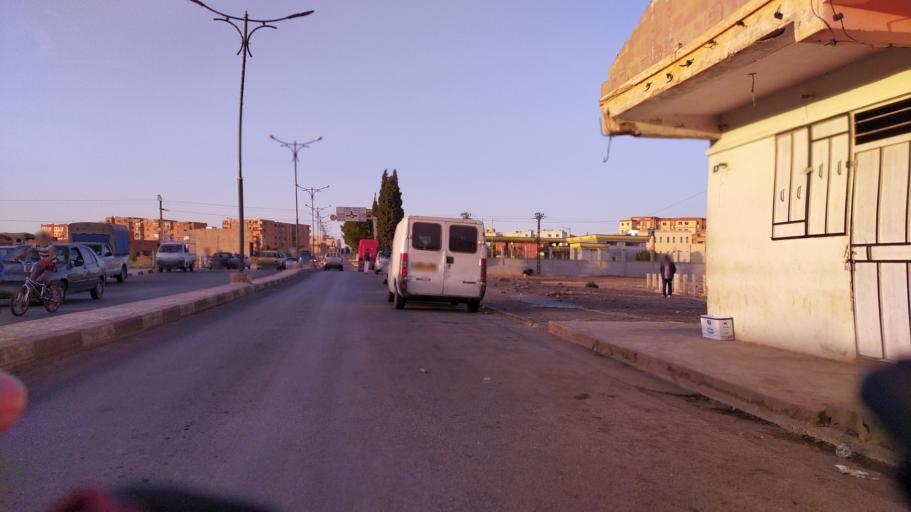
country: DZ
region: Tiaret
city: Frenda
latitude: 34.8948
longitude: 1.2472
